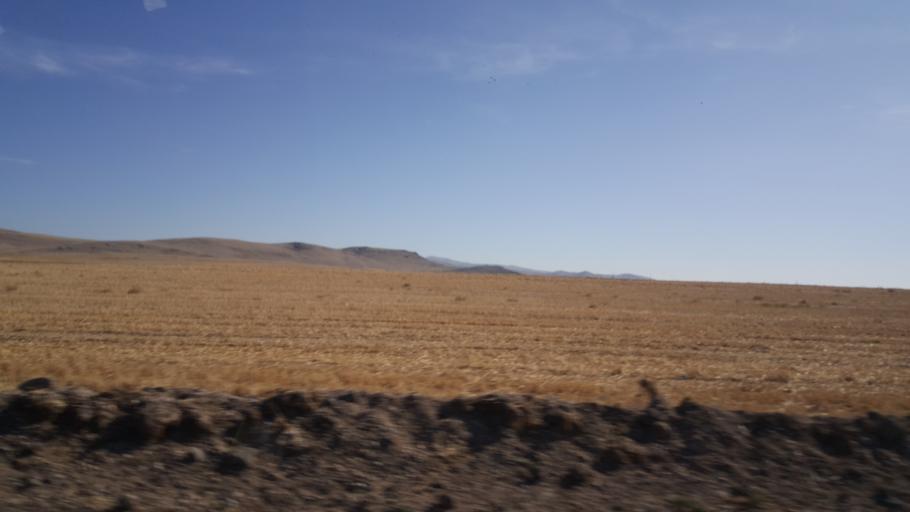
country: TR
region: Ankara
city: Yenice
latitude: 39.3511
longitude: 32.7733
